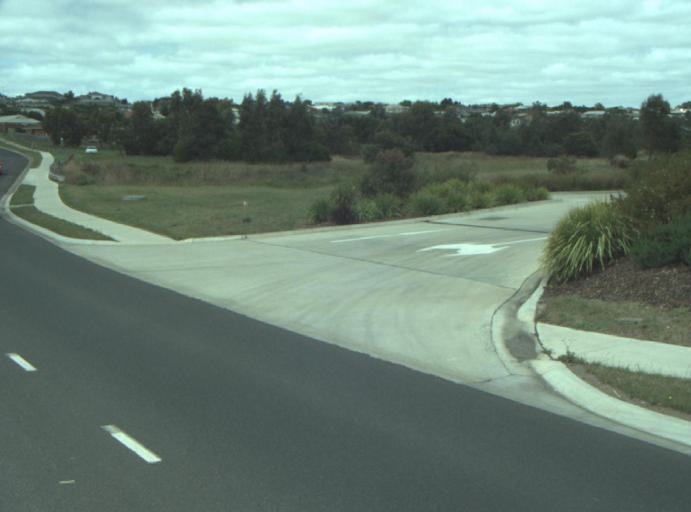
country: AU
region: Victoria
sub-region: Greater Geelong
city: Wandana Heights
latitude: -38.2028
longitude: 144.3125
